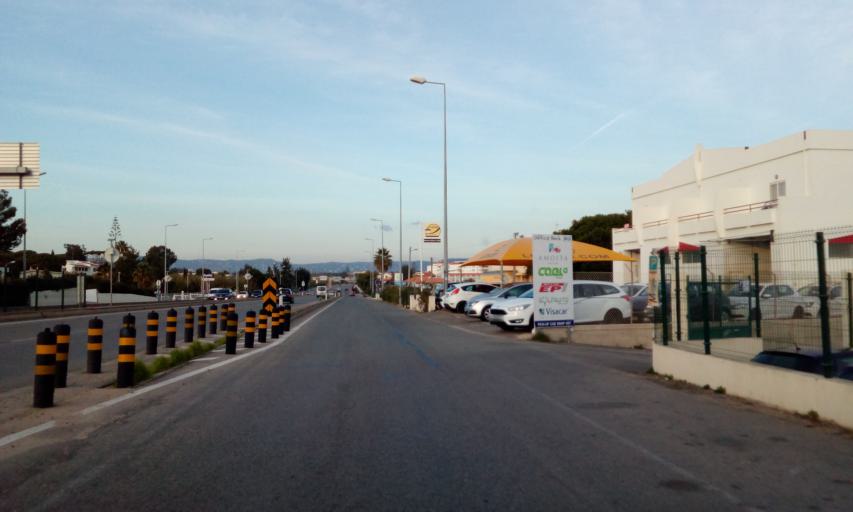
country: PT
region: Faro
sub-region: Faro
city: Faro
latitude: 37.0247
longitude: -7.9697
